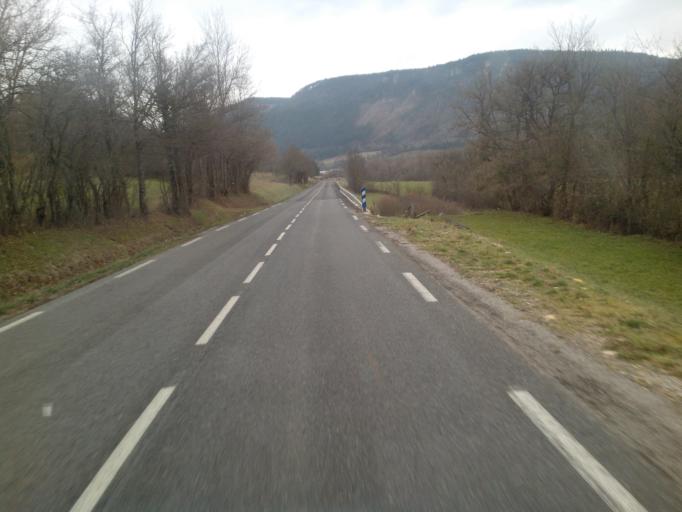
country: FR
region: Languedoc-Roussillon
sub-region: Departement de la Lozere
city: Mende
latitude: 44.4638
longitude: 3.5178
